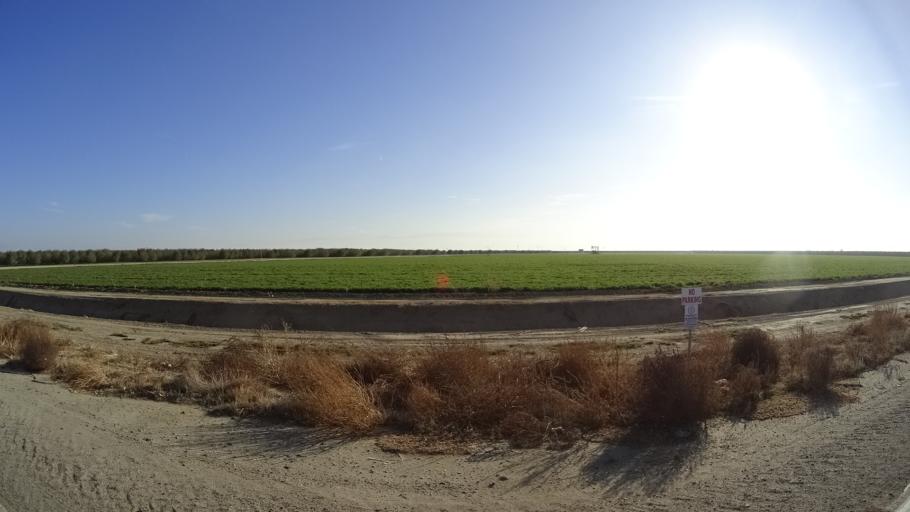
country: US
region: California
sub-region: Kern County
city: Rosedale
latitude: 35.2962
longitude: -119.1409
